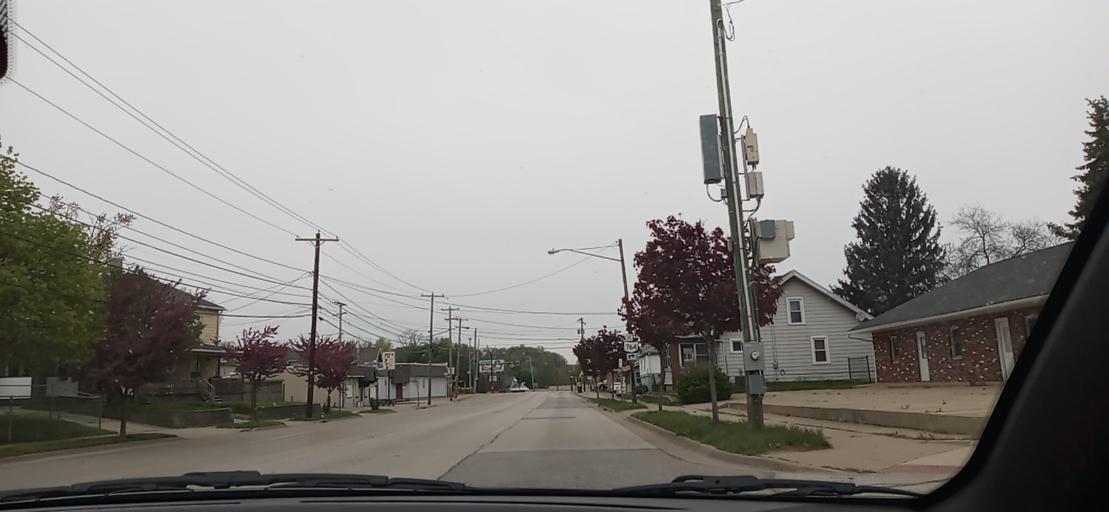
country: US
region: Ohio
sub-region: Summit County
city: Portage Lakes
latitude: 41.0373
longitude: -81.5458
